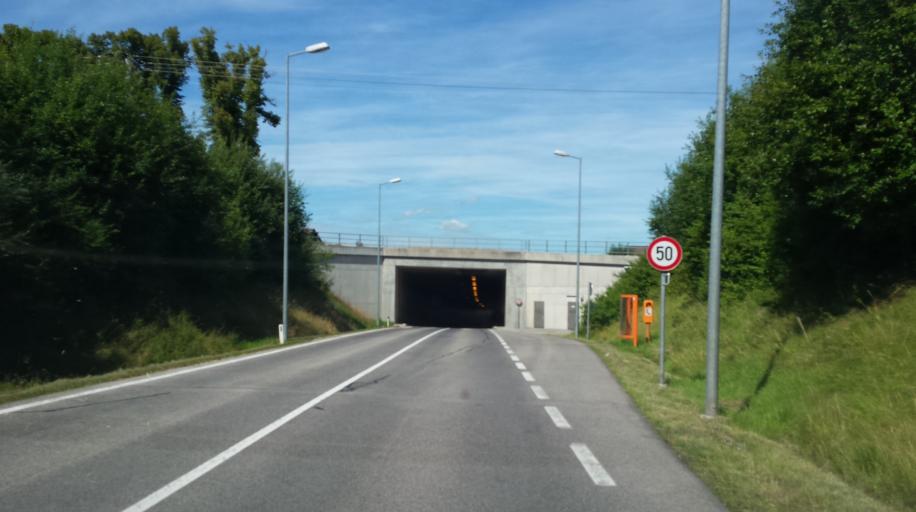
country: AT
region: Upper Austria
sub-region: Politischer Bezirk Vocklabruck
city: Sankt Georgen im Attergau
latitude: 47.9392
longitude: 13.4783
